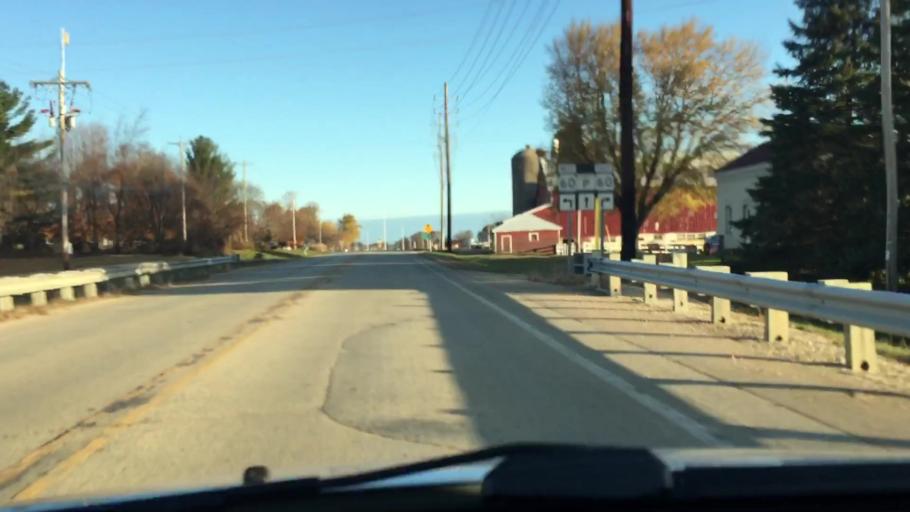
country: US
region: Wisconsin
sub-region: Washington County
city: Hartford
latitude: 43.3222
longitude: -88.4590
